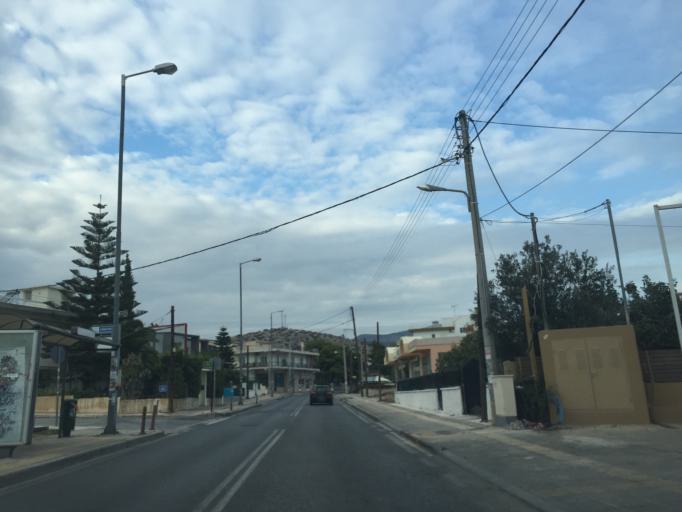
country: GR
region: Attica
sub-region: Nomarchia Anatolikis Attikis
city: Vari
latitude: 37.8288
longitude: 23.8033
